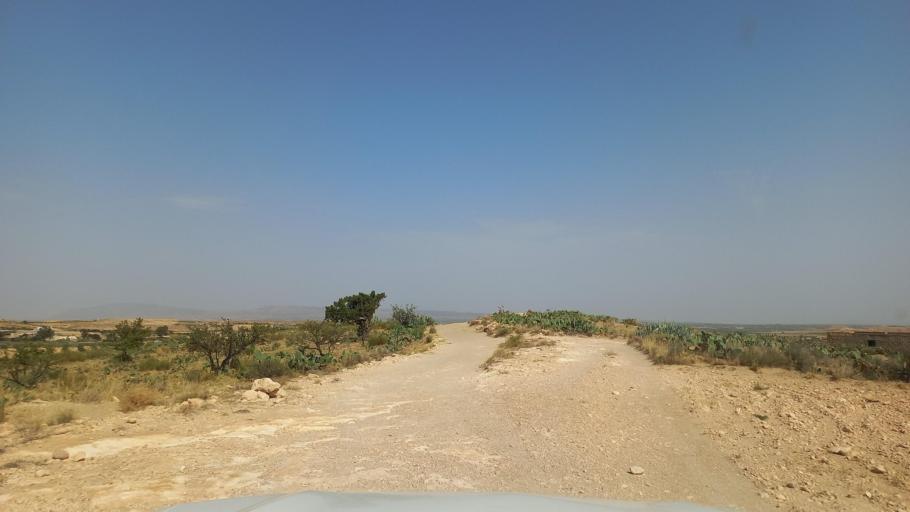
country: TN
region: Al Qasrayn
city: Kasserine
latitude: 35.2992
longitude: 8.9427
